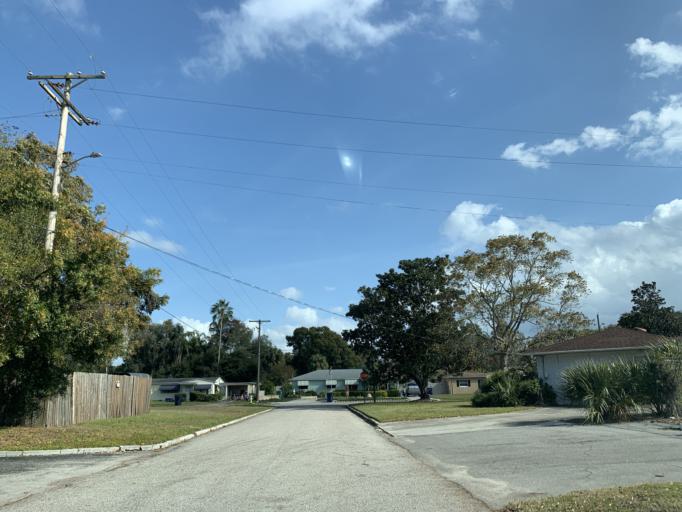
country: US
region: Florida
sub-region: Hillsborough County
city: Tampa
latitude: 27.9030
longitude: -82.5176
